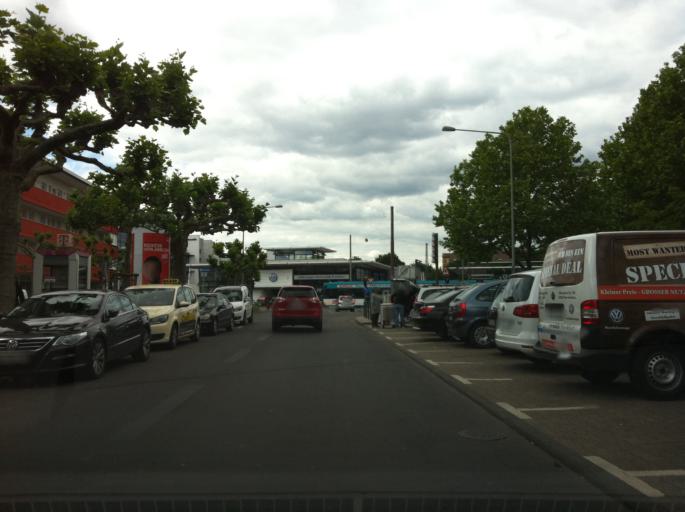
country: DE
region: Hesse
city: Niederrad
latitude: 50.1004
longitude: 8.6255
